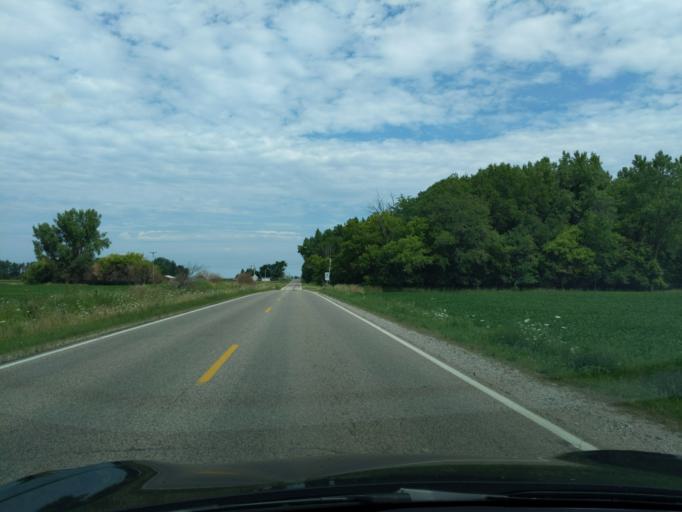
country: US
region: Michigan
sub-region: Gratiot County
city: Breckenridge
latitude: 43.2931
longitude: -84.4290
